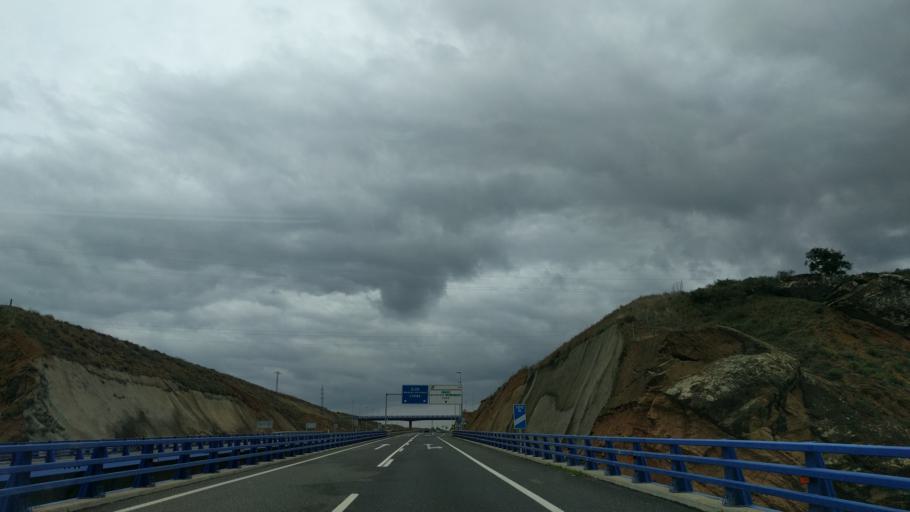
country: ES
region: Aragon
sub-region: Provincia de Huesca
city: Castejon del Puente
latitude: 41.9545
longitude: 0.1817
